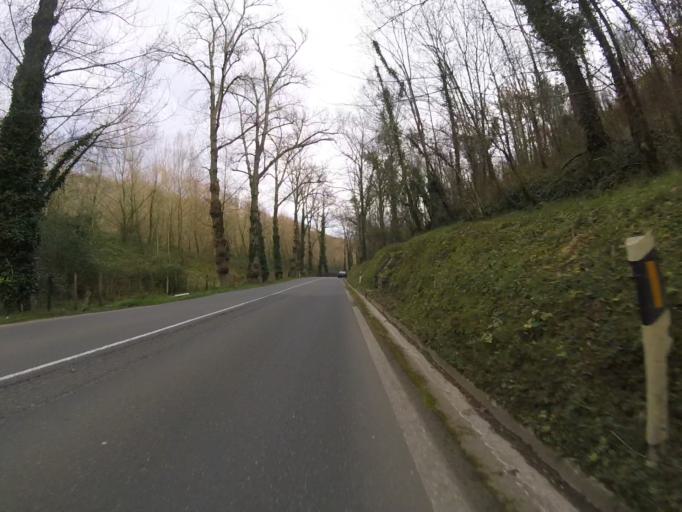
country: ES
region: Basque Country
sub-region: Provincia de Guipuzcoa
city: Aizarnazabal
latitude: 43.2533
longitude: -2.2484
